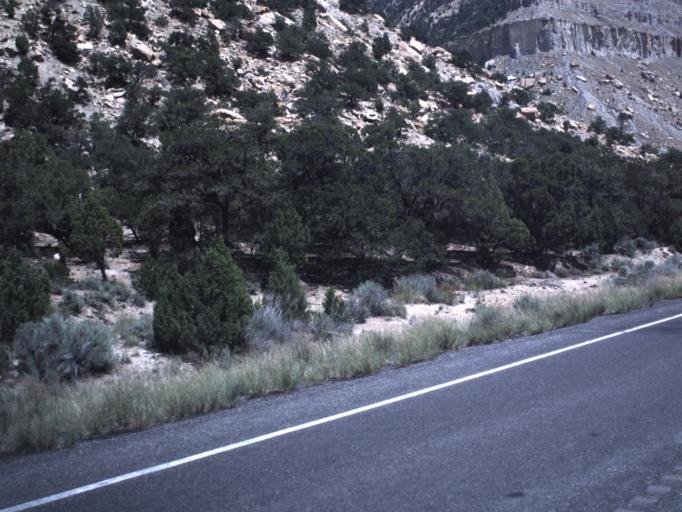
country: US
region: Utah
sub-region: Emery County
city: Huntington
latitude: 39.3944
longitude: -111.1038
